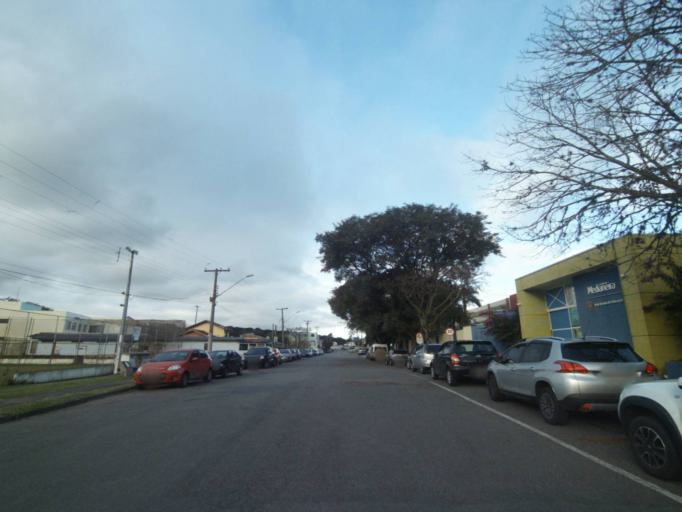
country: BR
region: Parana
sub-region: Curitiba
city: Curitiba
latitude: -25.4503
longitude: -49.2482
